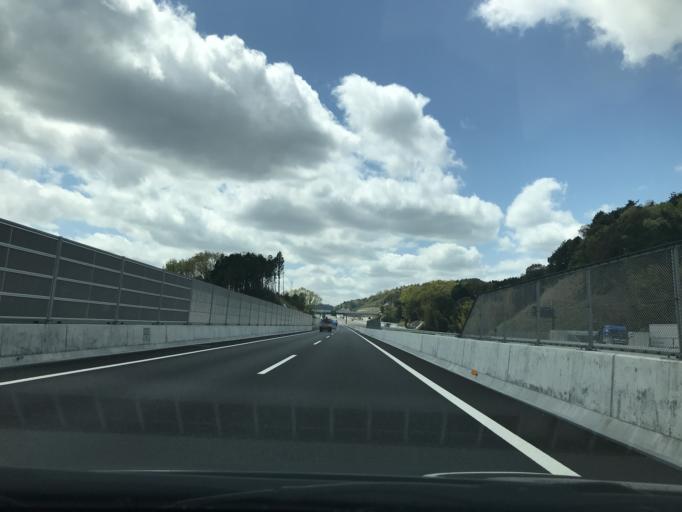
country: JP
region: Osaka
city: Ibaraki
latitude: 34.8894
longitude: 135.5410
